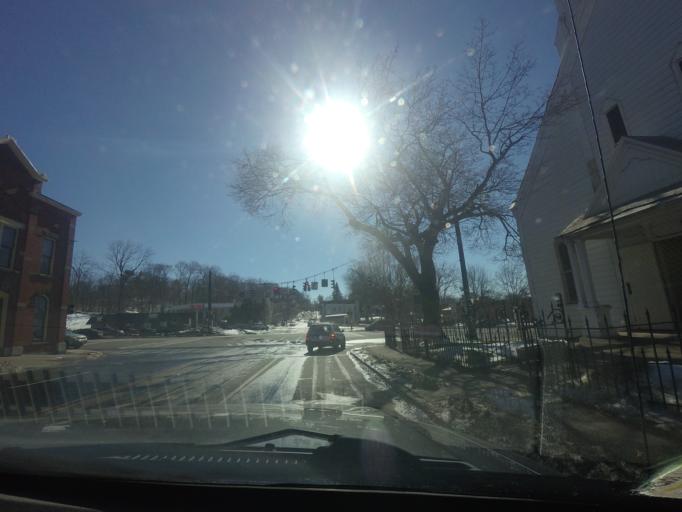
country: US
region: New York
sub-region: Albany County
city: Green Island
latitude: 42.7398
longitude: -73.6797
